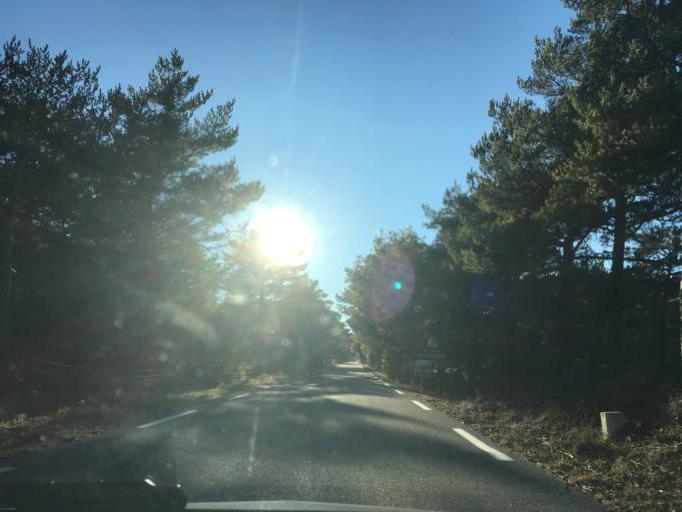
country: FR
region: Provence-Alpes-Cote d'Azur
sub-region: Departement du Var
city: Villecroze
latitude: 43.5999
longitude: 6.3356
